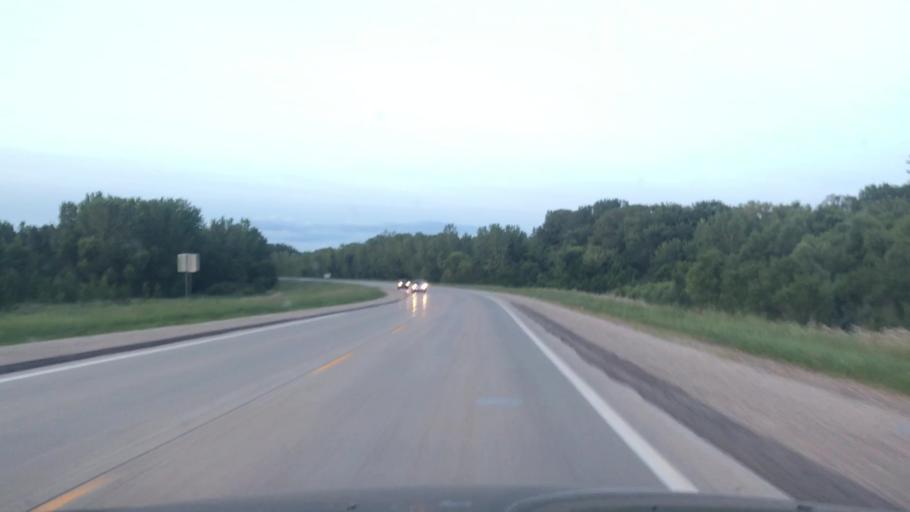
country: US
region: Minnesota
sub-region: Redwood County
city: Redwood Falls
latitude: 44.5420
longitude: -95.0001
